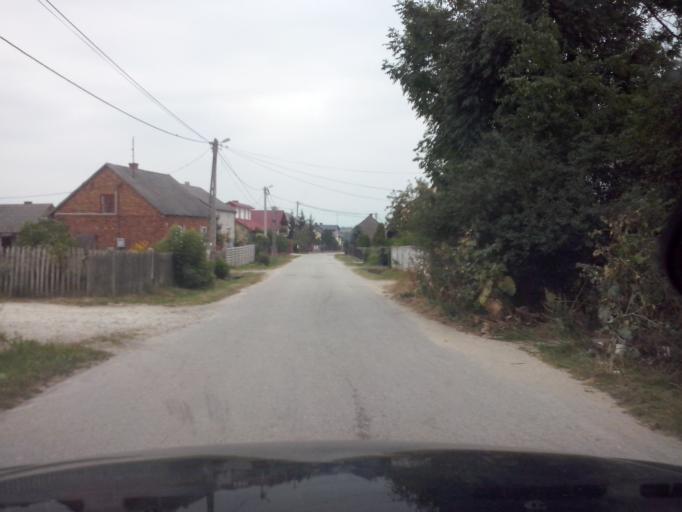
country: PL
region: Swietokrzyskie
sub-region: Powiat kielecki
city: Morawica
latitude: 50.6927
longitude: 20.5727
